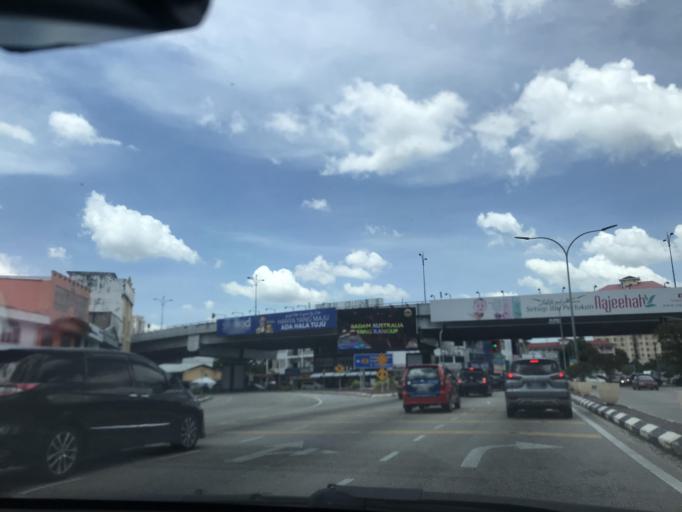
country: MY
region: Kelantan
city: Kota Bharu
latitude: 6.1180
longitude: 102.2420
